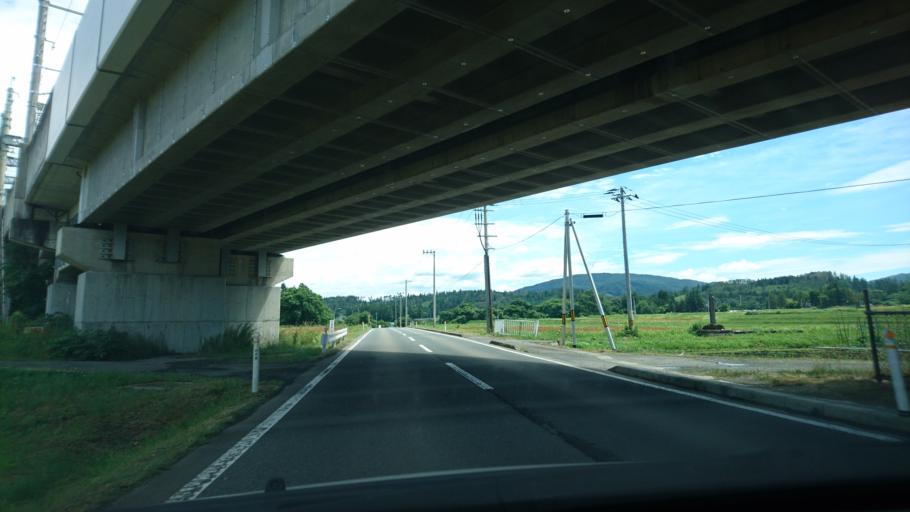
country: JP
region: Iwate
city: Hanamaki
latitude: 39.4222
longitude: 141.1774
